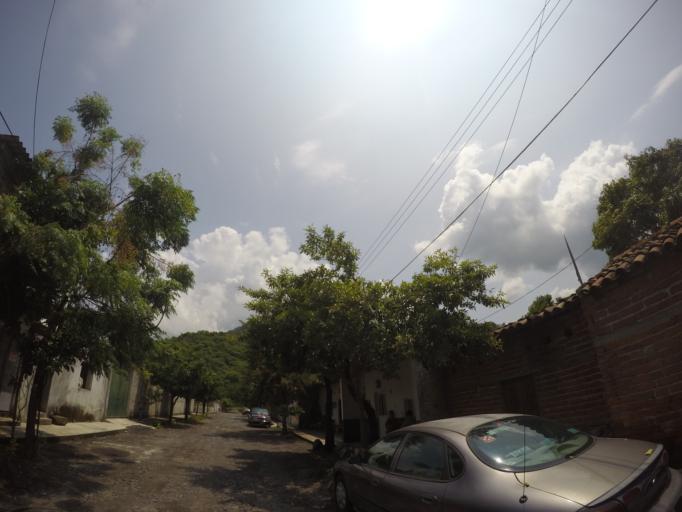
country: MX
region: Nayarit
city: Jala
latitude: 21.1048
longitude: -104.4328
